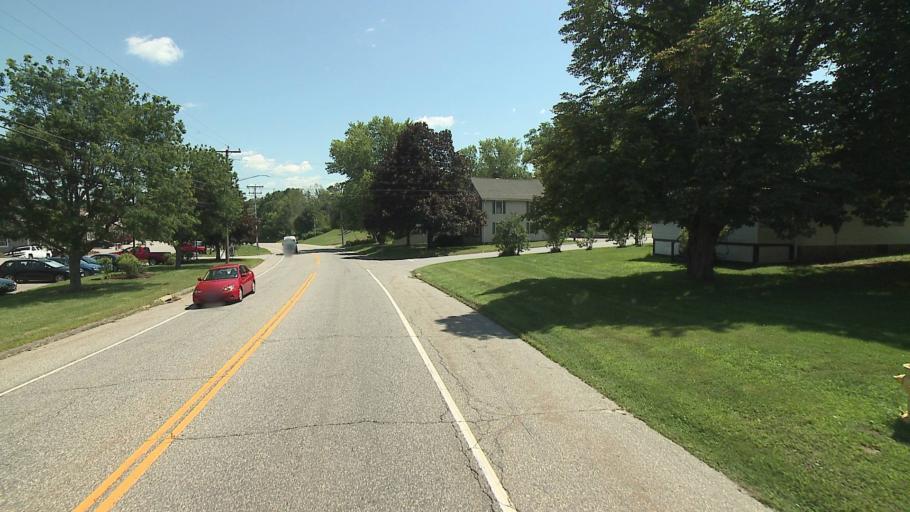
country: US
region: Connecticut
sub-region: Litchfield County
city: Northwest Harwinton
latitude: 41.8006
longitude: -73.0899
